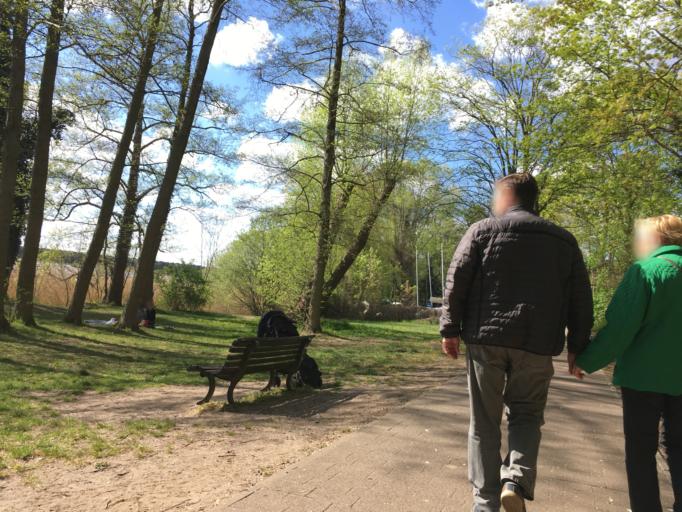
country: DE
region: Brandenburg
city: Wandlitz
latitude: 52.7606
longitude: 13.4673
